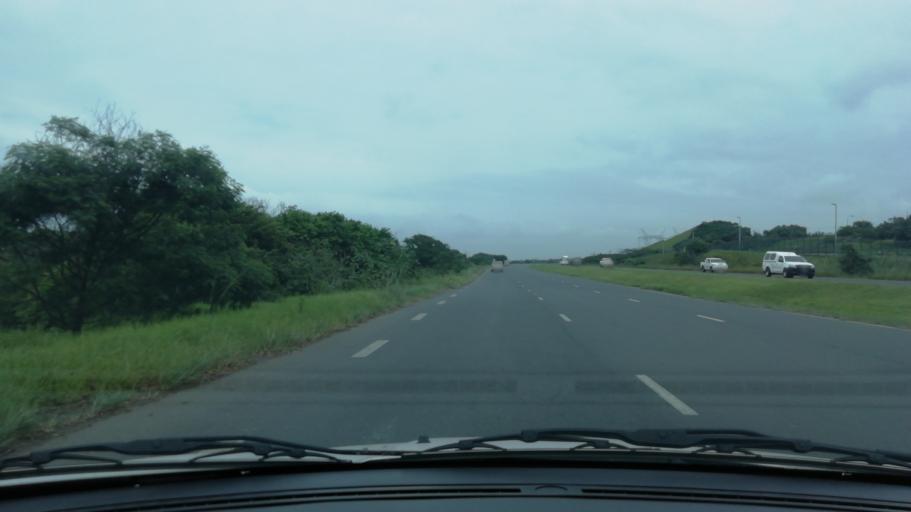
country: ZA
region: KwaZulu-Natal
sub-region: uThungulu District Municipality
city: Richards Bay
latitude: -28.7713
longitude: 32.0305
